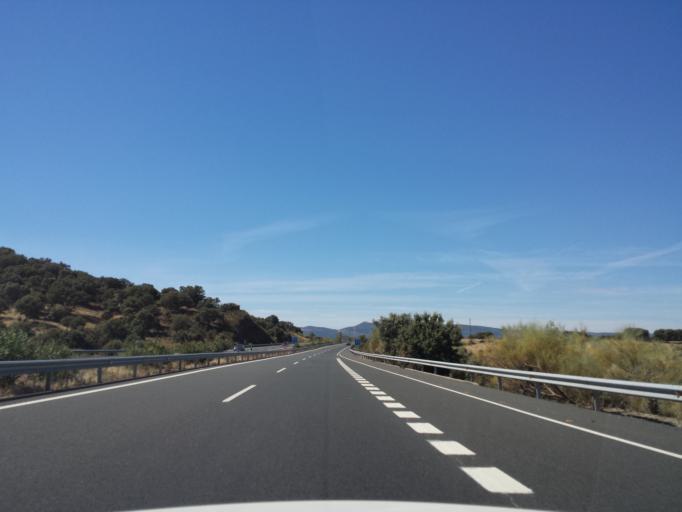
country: ES
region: Extremadura
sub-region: Provincia de Caceres
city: Almaraz
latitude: 39.8040
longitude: -5.6726
